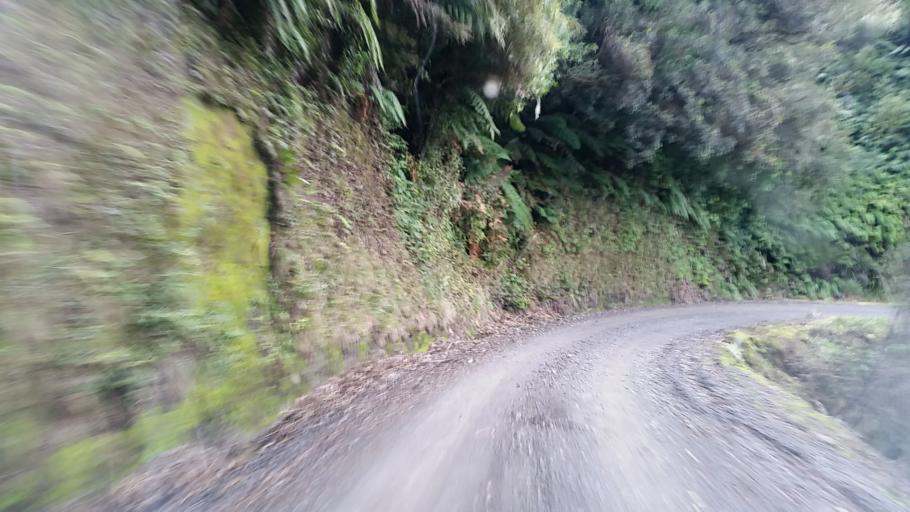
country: NZ
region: Taranaki
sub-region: New Plymouth District
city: Waitara
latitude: -39.1616
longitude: 174.5506
